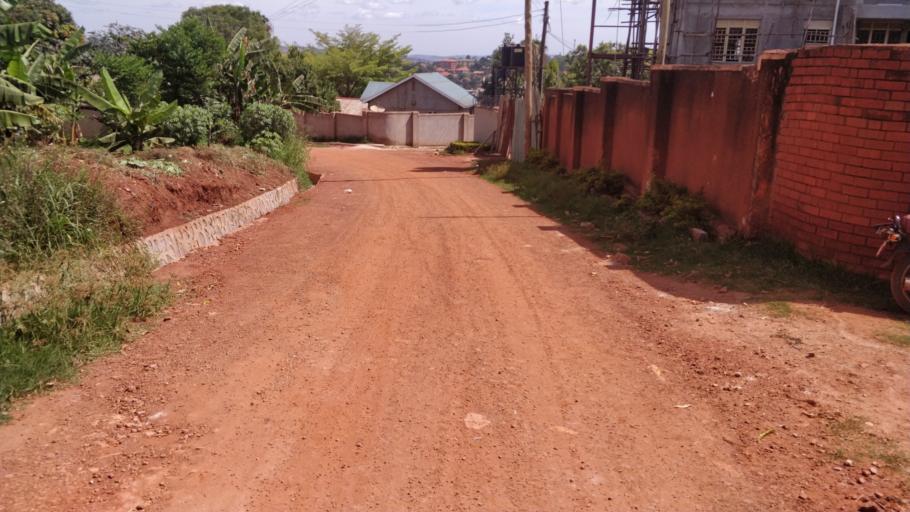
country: UG
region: Central Region
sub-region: Kampala District
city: Kampala
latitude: 0.2682
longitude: 32.6110
